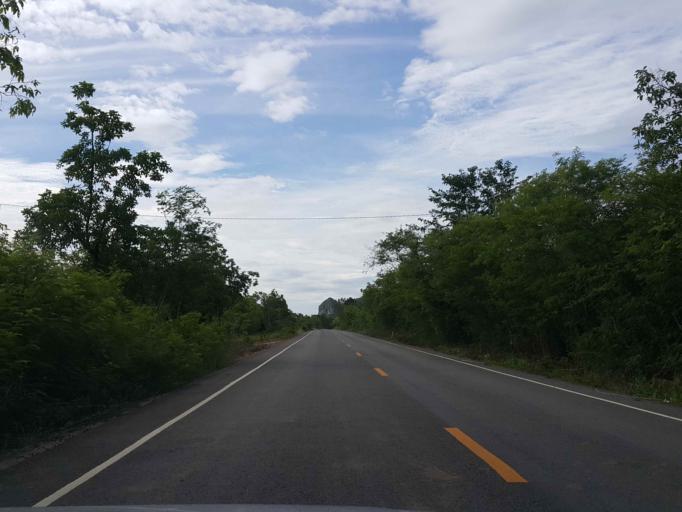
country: TH
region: Sukhothai
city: Thung Saliam
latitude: 17.2793
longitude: 99.5285
